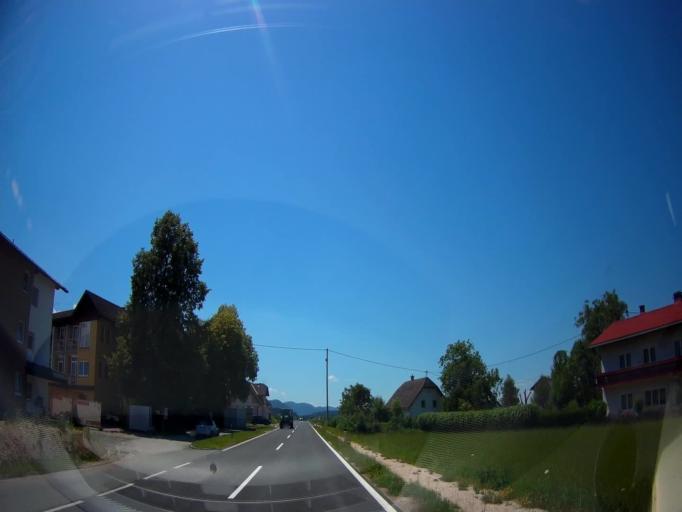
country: AT
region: Carinthia
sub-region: Politischer Bezirk Volkermarkt
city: Eberndorf
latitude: 46.6174
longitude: 14.5986
